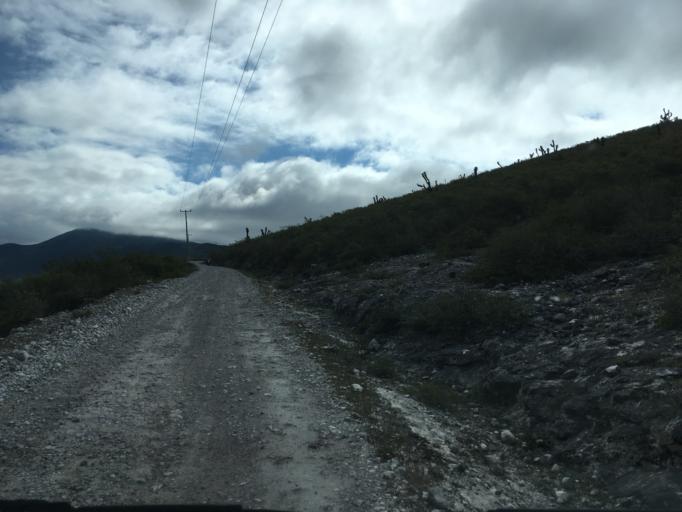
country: MX
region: Hidalgo
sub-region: Metztitlan
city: Fontezuelas
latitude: 20.6432
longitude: -98.8517
